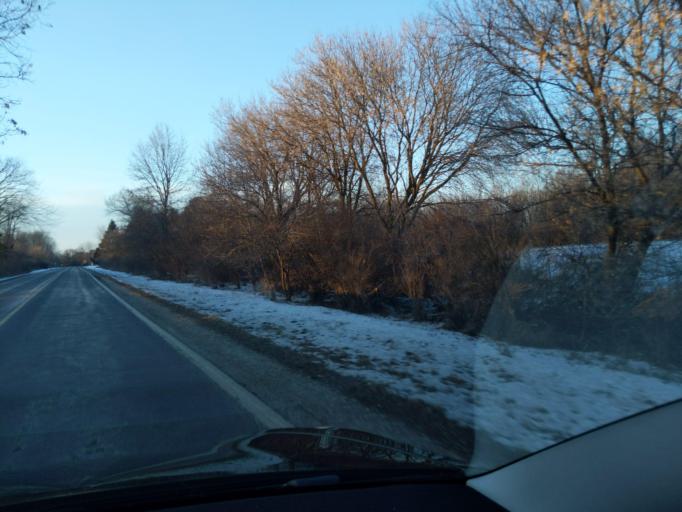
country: US
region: Michigan
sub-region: Ingham County
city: Mason
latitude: 42.5391
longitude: -84.3521
